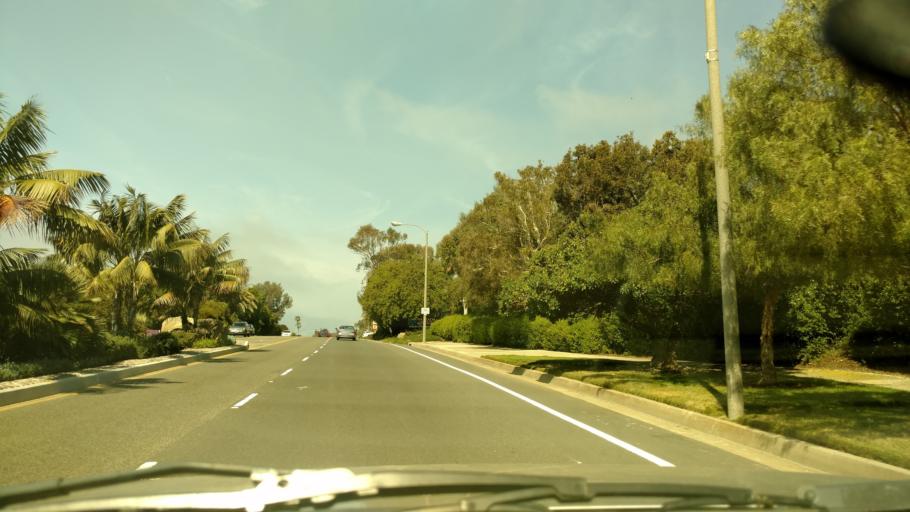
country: US
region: California
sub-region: Orange County
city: Laguna Niguel
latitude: 33.4907
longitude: -117.7317
